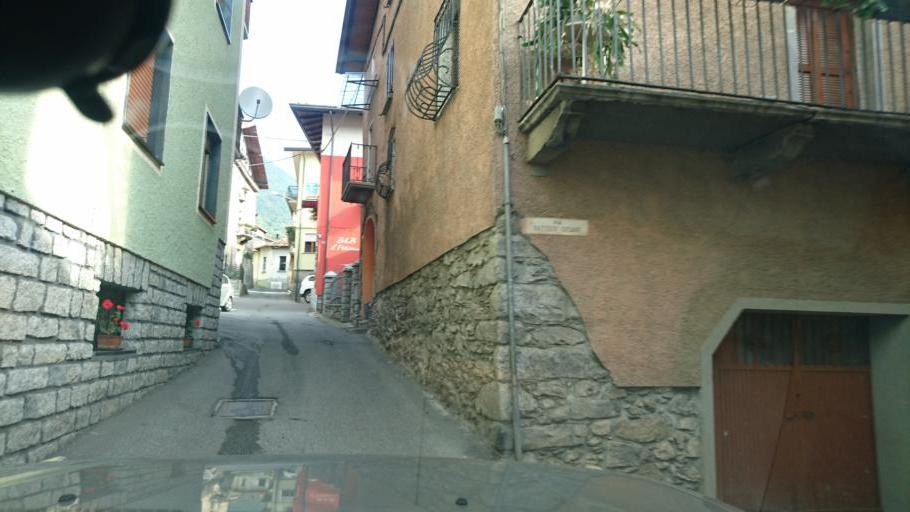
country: IT
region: Lombardy
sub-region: Provincia di Brescia
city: Malonno
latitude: 46.1179
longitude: 10.3135
